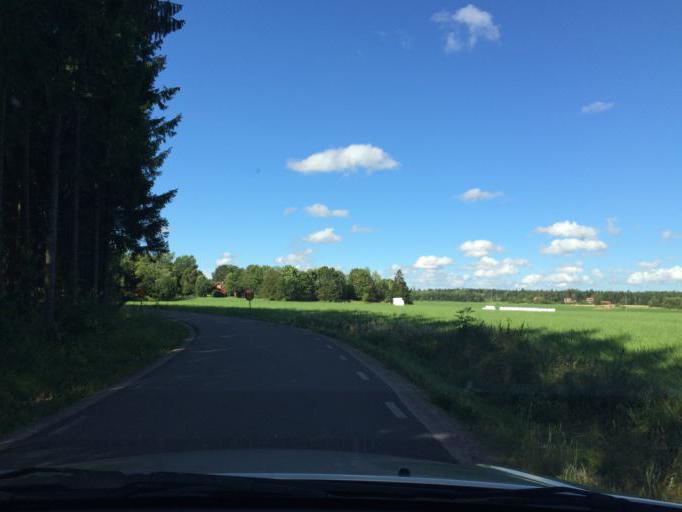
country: SE
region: Soedermanland
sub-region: Eskilstuna Kommun
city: Kvicksund
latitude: 59.4960
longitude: 16.3461
